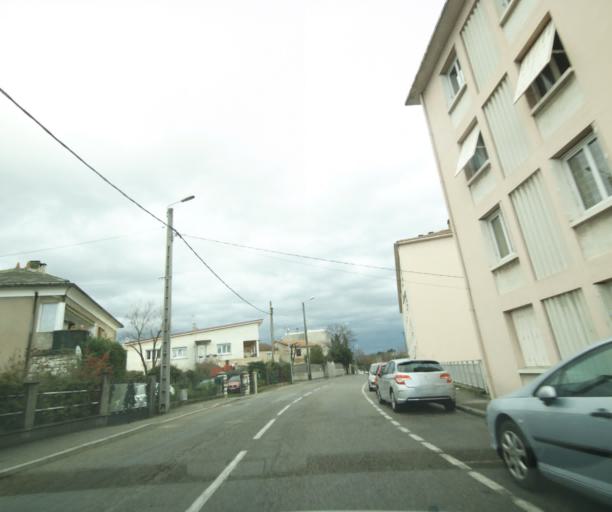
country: FR
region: Rhone-Alpes
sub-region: Departement de la Drome
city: Bourg-les-Valence
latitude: 44.9538
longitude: 4.9013
